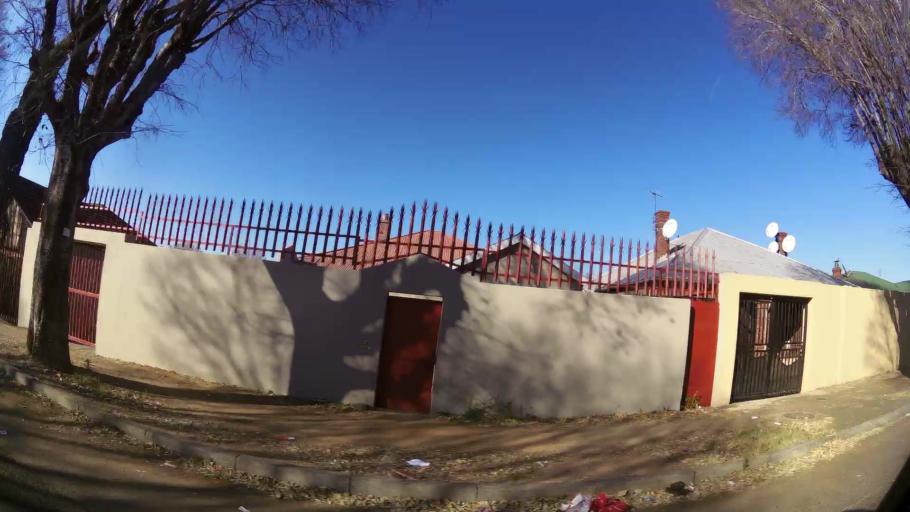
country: ZA
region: Gauteng
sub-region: City of Johannesburg Metropolitan Municipality
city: Johannesburg
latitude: -26.2017
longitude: 28.0991
